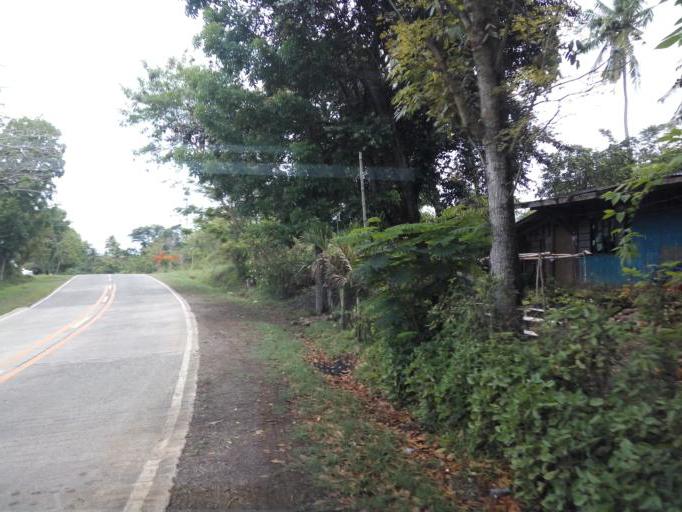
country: PH
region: Cagayan Valley
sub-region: Province of Quirino
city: Saguday
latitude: 16.5296
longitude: 121.5205
